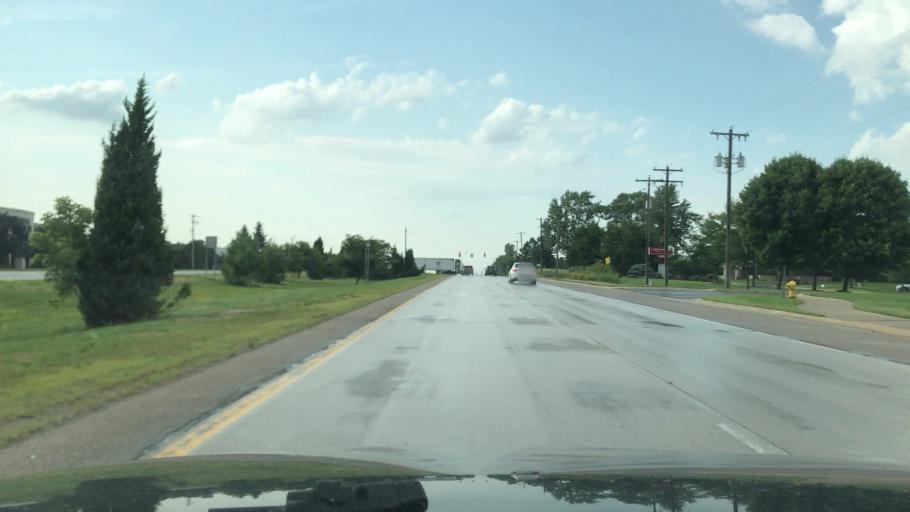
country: US
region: Michigan
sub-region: Kent County
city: East Grand Rapids
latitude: 42.8751
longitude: -85.5583
